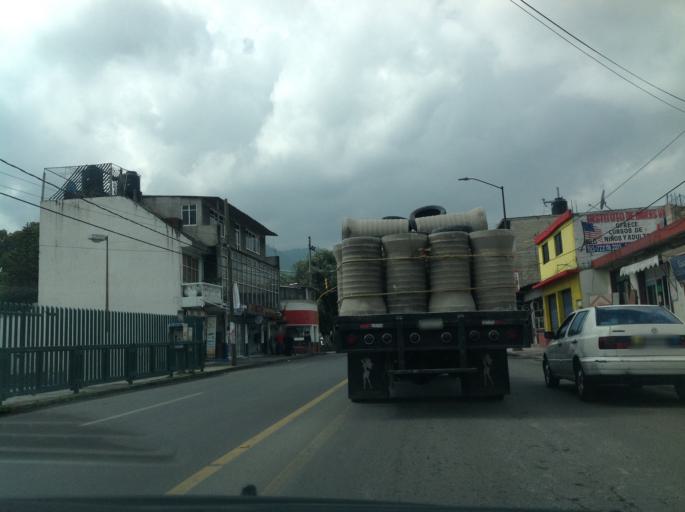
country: MX
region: Morelos
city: Tenango de Arista
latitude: 19.1040
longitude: -99.5867
